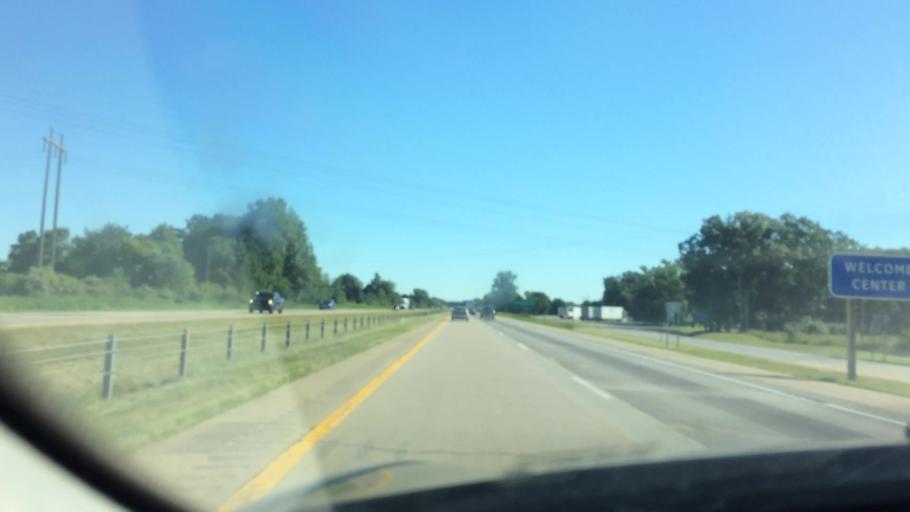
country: US
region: Michigan
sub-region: Monroe County
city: Petersburg
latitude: 41.8293
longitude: -83.6799
